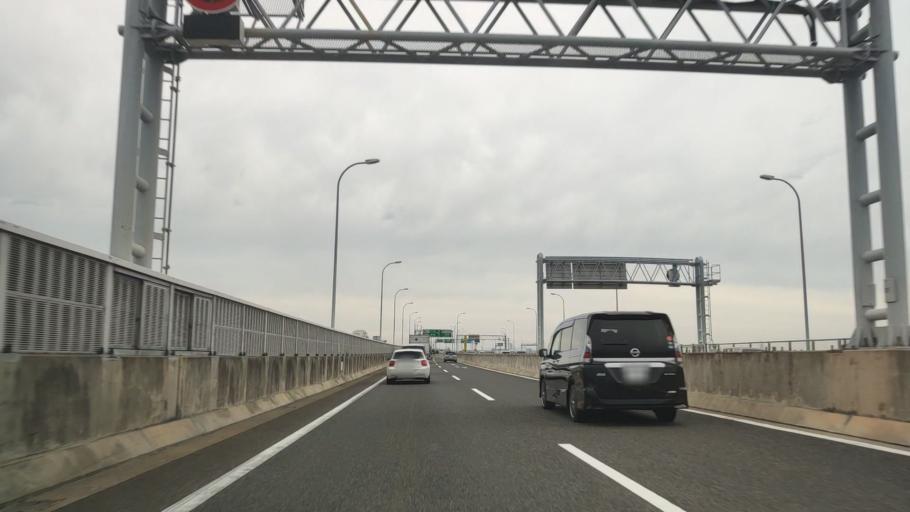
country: JP
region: Aichi
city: Iwakura
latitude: 35.2673
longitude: 136.8356
